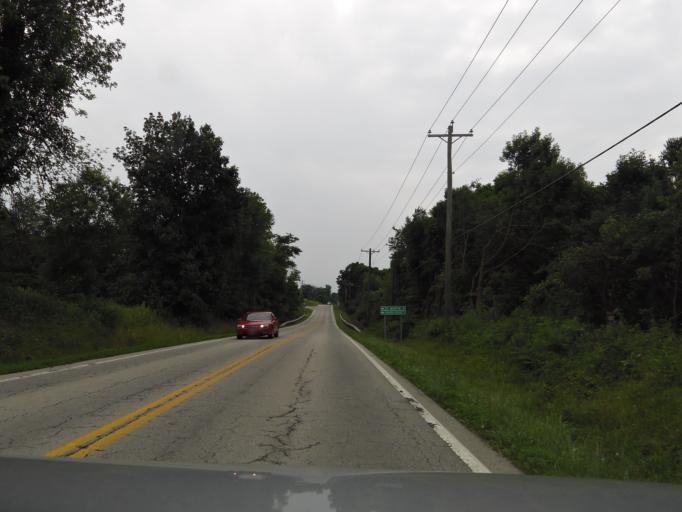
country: US
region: Ohio
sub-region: Clinton County
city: Blanchester
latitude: 39.2592
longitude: -83.9033
